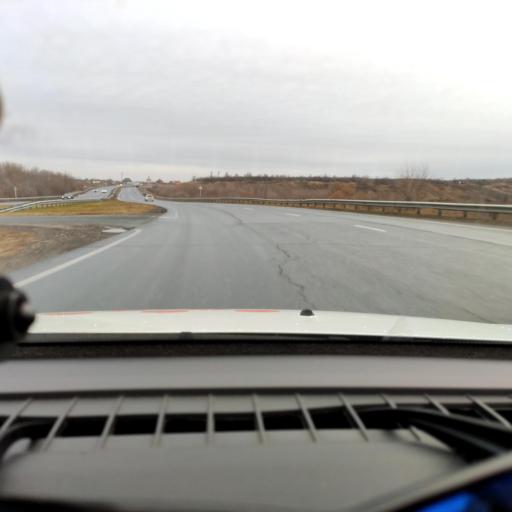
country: RU
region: Samara
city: Novokuybyshevsk
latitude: 53.0575
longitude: 50.0190
